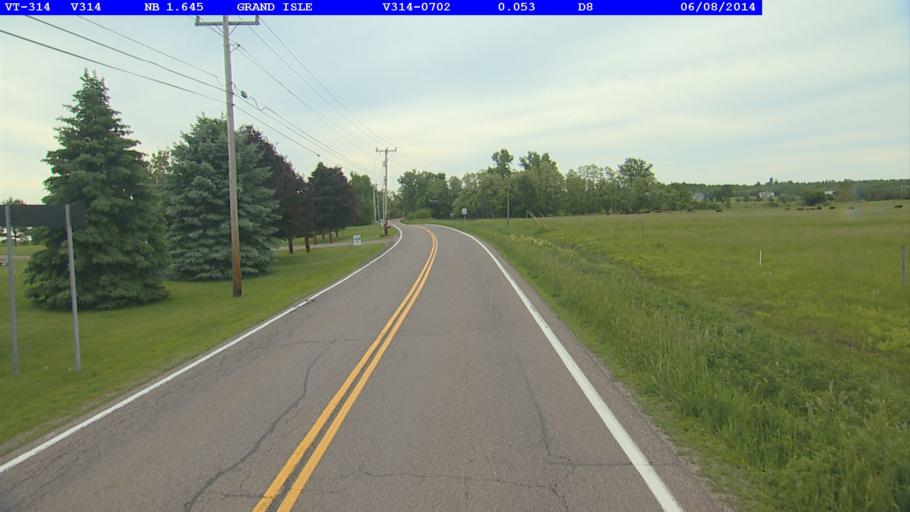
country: US
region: New York
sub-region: Clinton County
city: Cumberland Head
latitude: 44.6782
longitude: -73.3470
